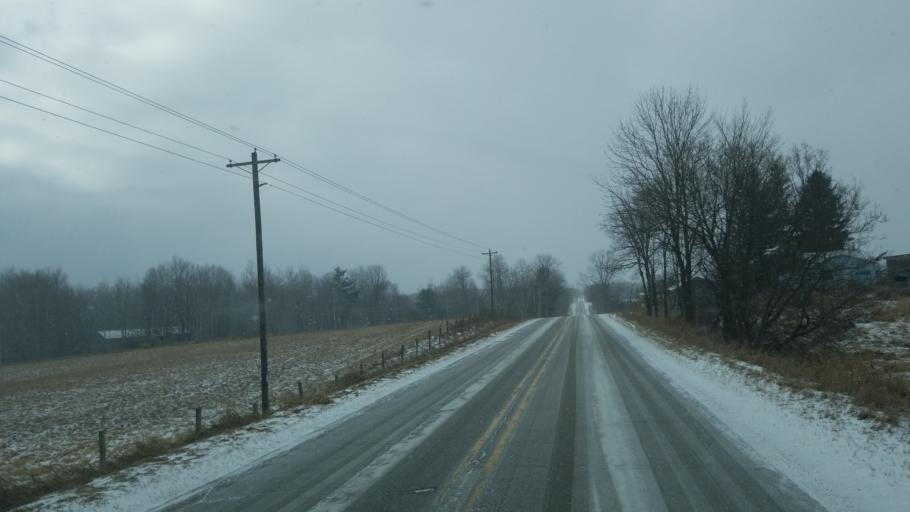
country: US
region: Michigan
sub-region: Osceola County
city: Evart
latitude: 44.0303
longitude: -85.2144
